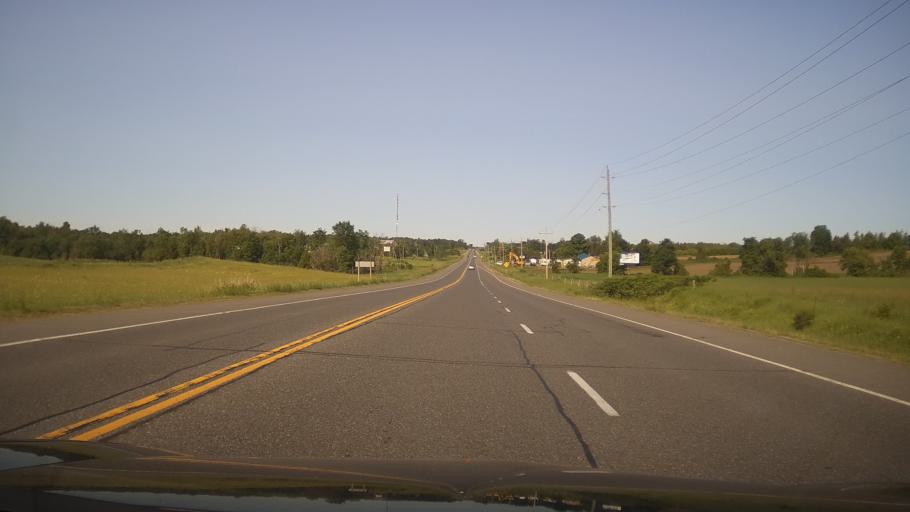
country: CA
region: Ontario
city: Peterborough
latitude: 44.3600
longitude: -78.0274
